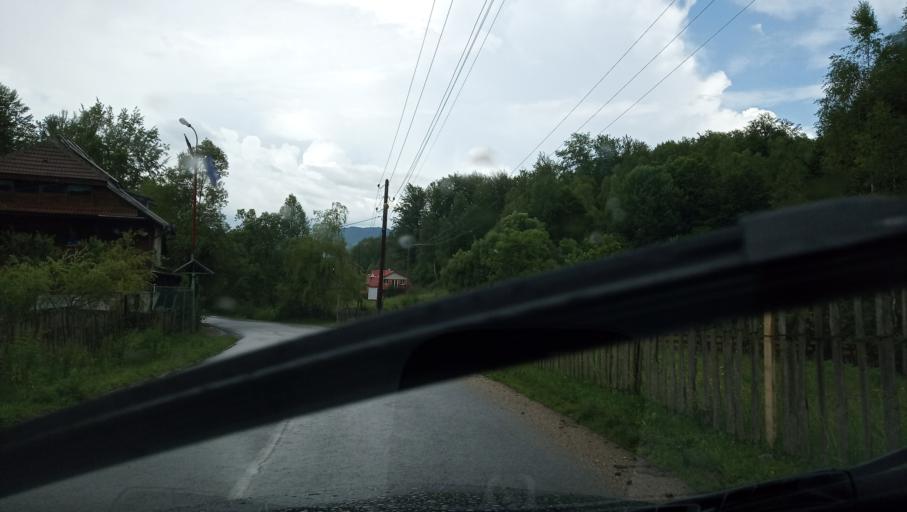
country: RO
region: Hunedoara
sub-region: Oras Petrila
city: Petrila
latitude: 45.4032
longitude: 23.4141
